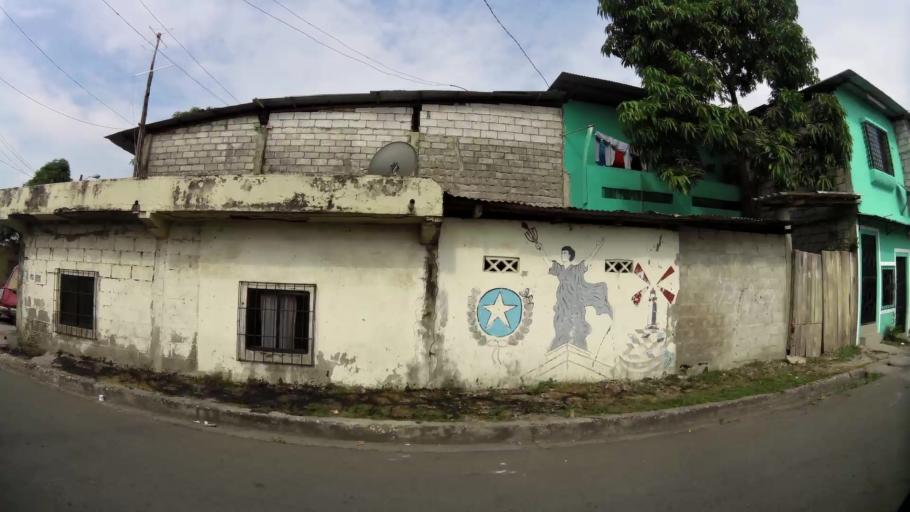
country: EC
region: Guayas
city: Guayaquil
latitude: -2.2554
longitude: -79.9063
